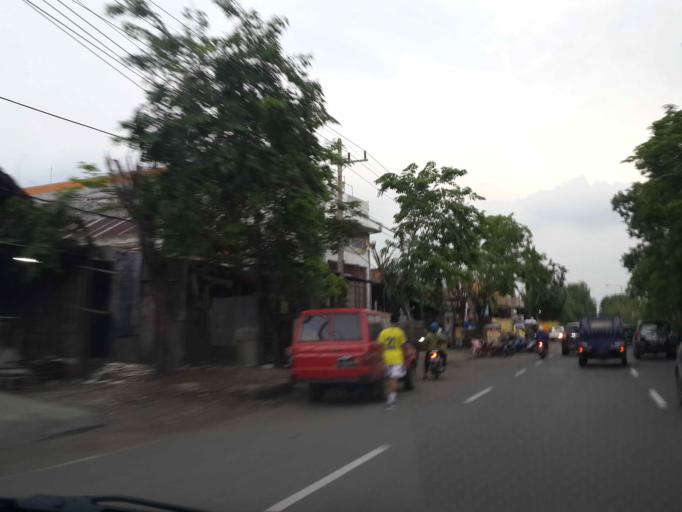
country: ID
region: East Java
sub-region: Kota Surabaya
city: Surabaya
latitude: -7.2502
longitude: 112.7208
